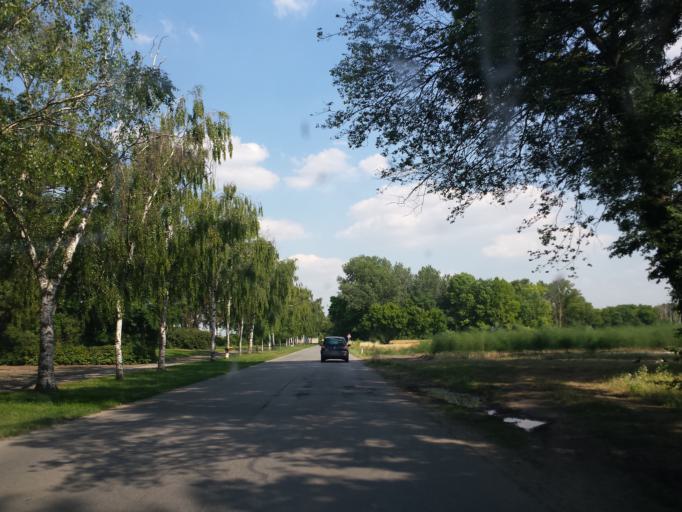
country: AT
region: Lower Austria
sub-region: Politischer Bezirk Ganserndorf
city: Aderklaa
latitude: 48.2848
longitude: 16.5409
